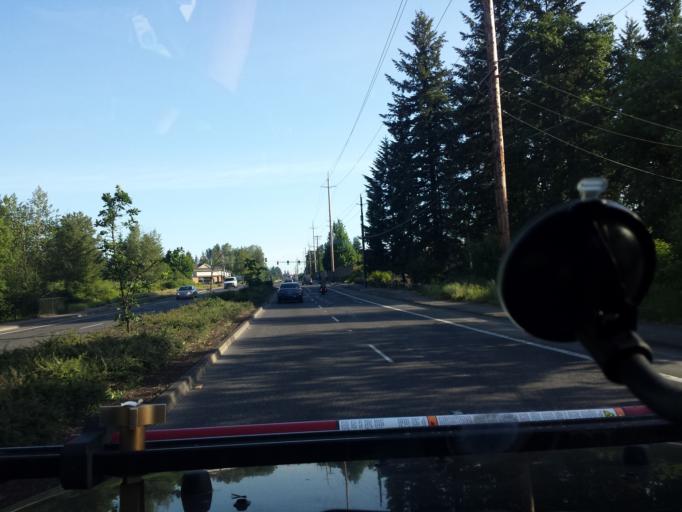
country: US
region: Washington
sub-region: Clark County
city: Mill Plain
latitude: 45.6681
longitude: -122.5059
